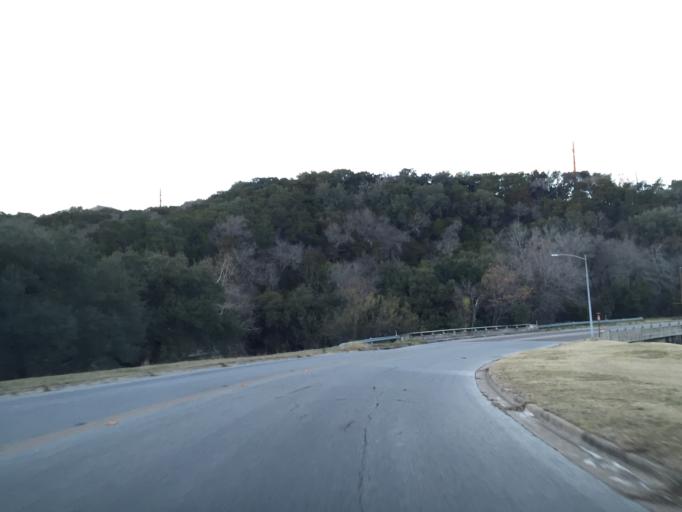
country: US
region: Texas
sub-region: Williamson County
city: Jollyville
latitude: 30.3987
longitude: -97.7629
